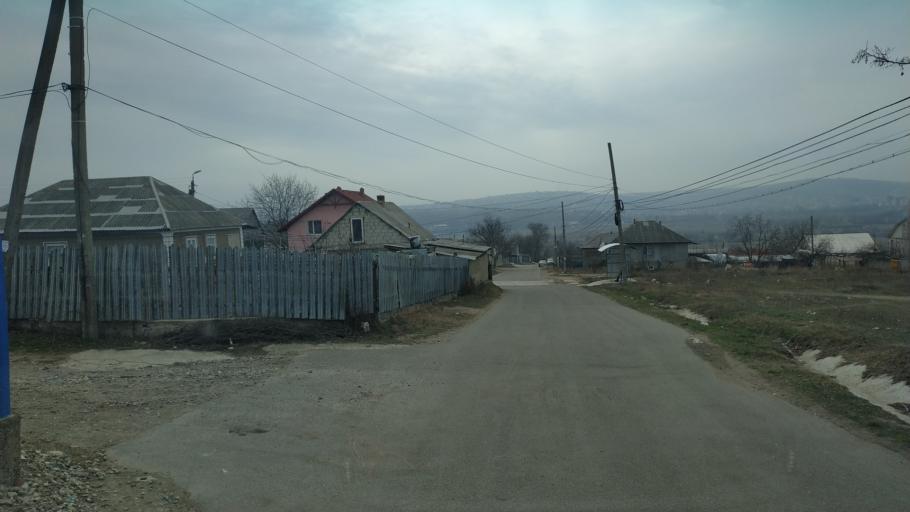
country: MD
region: Chisinau
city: Singera
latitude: 46.9366
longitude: 28.9847
